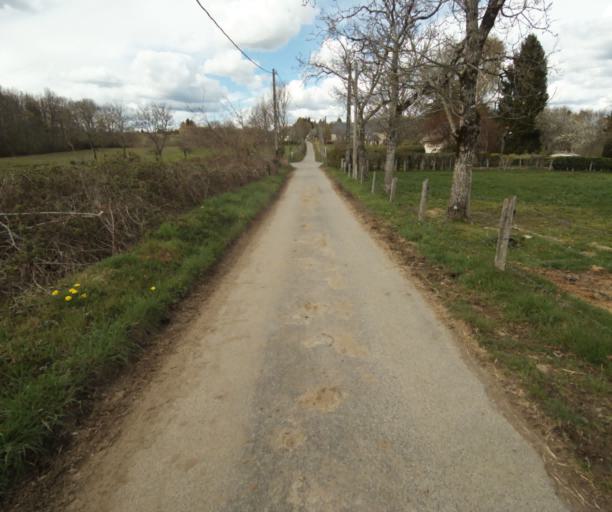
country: FR
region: Limousin
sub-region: Departement de la Correze
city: Argentat
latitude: 45.1818
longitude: 1.9222
